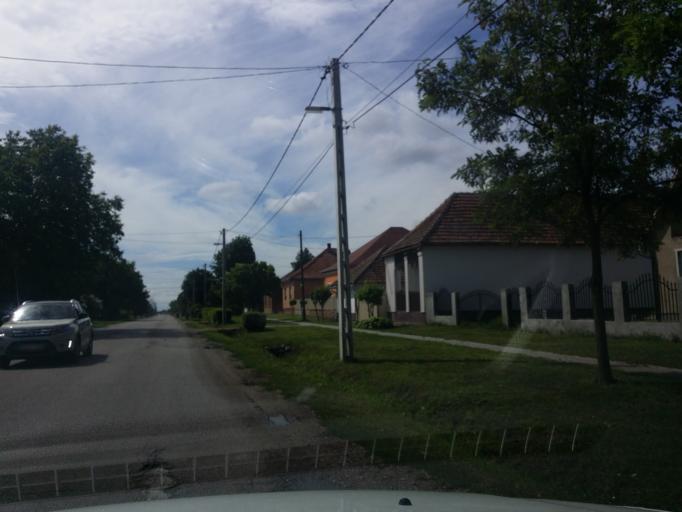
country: HU
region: Heves
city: Besenyotelek
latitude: 47.6039
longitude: 20.4426
